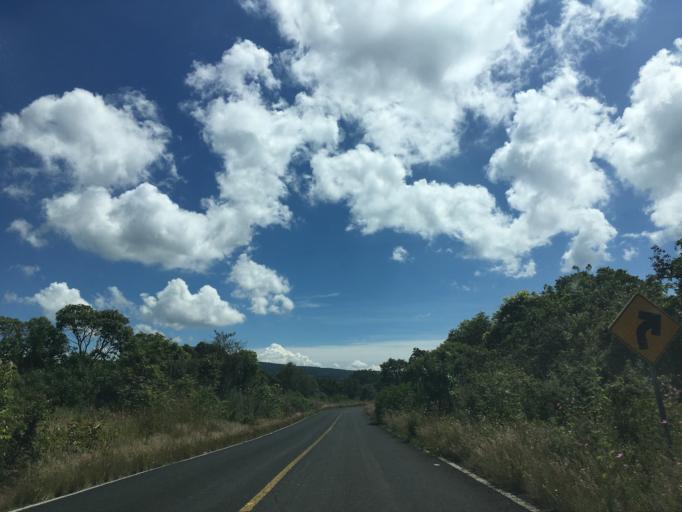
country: MX
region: Michoacan
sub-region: Morelia
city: Cuto de la Esperanza
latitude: 19.7406
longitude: -101.3527
